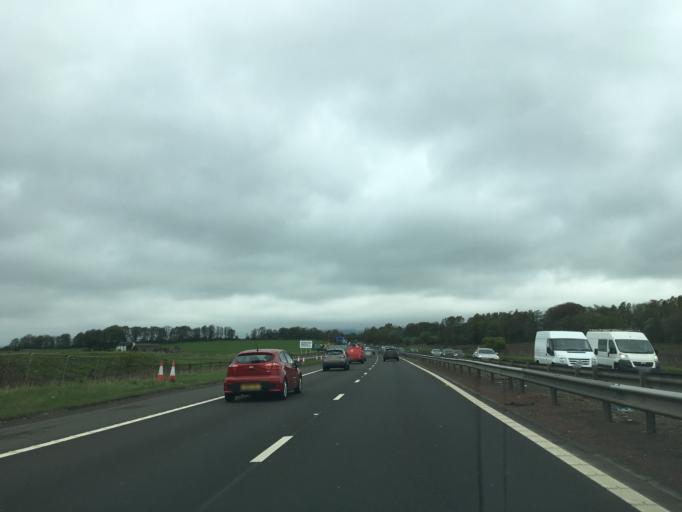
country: GB
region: Scotland
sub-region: Renfrewshire
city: Bishopton
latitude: 55.8924
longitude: -4.4814
